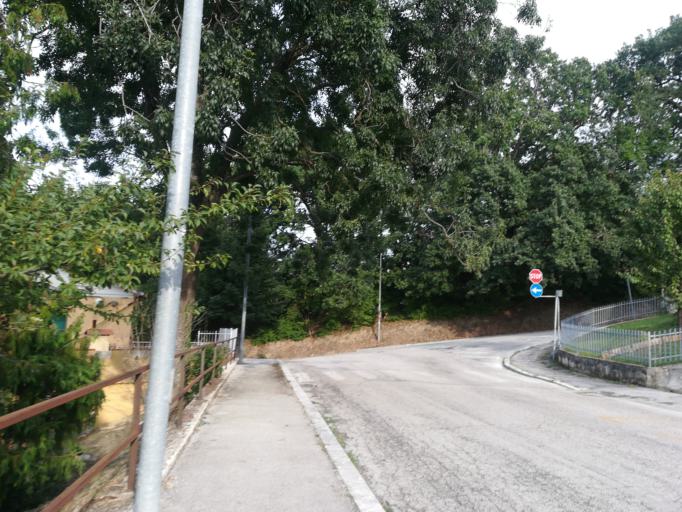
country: IT
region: The Marches
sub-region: Provincia di Macerata
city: Macerata
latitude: 43.3099
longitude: 13.4628
